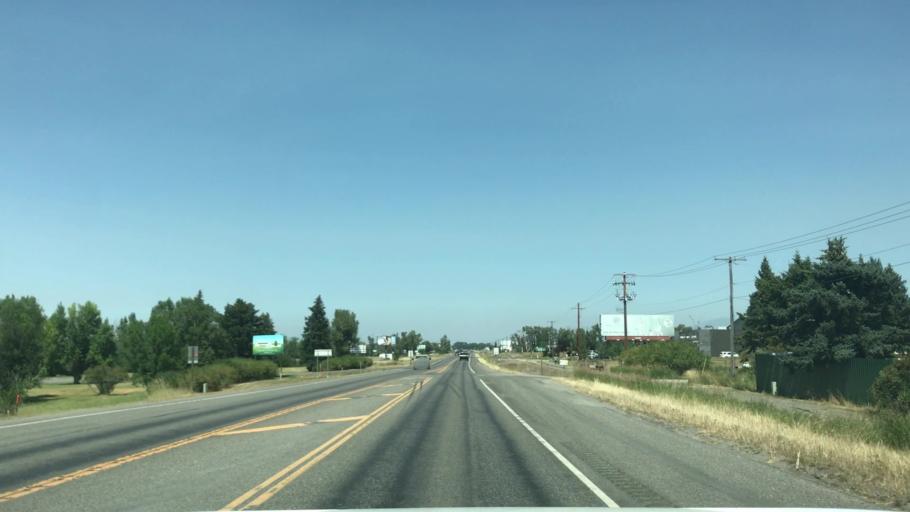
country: US
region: Montana
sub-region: Gallatin County
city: Four Corners
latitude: 45.5923
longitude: -111.1970
